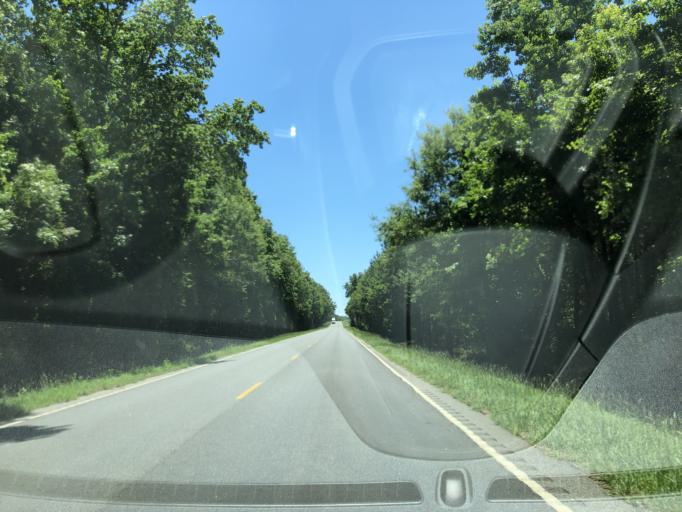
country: US
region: South Carolina
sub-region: Barnwell County
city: Blackville
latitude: 33.3621
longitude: -81.3090
